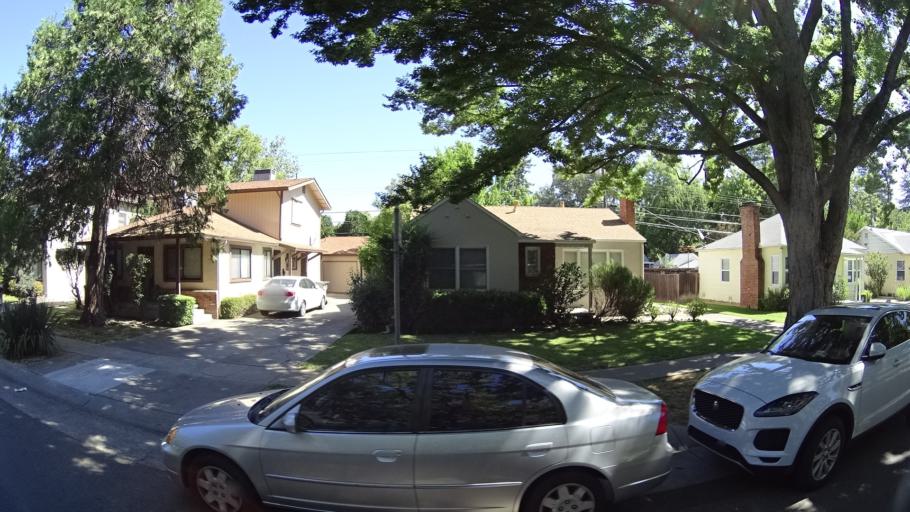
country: US
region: California
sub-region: Sacramento County
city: Sacramento
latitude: 38.5564
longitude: -121.4567
